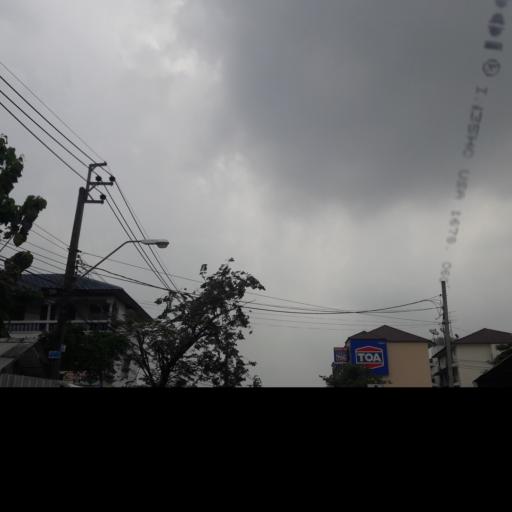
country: TH
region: Bangkok
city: Suan Luang
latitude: 13.7324
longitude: 100.6214
